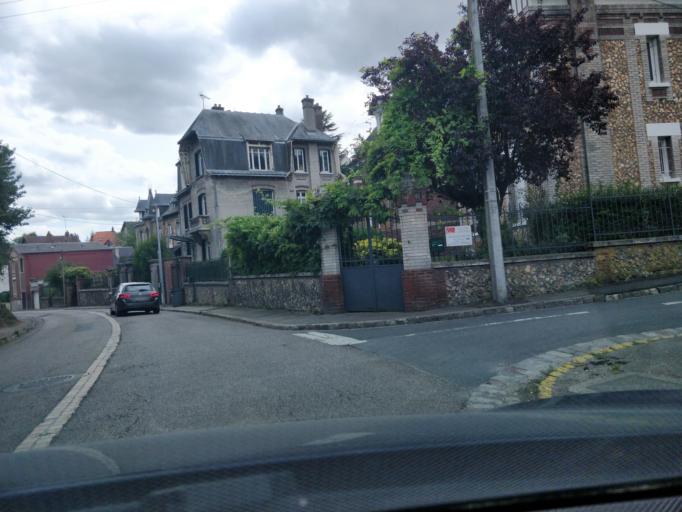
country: FR
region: Haute-Normandie
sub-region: Departement de la Seine-Maritime
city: Mont-Saint-Aignan
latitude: 49.4595
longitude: 1.0934
